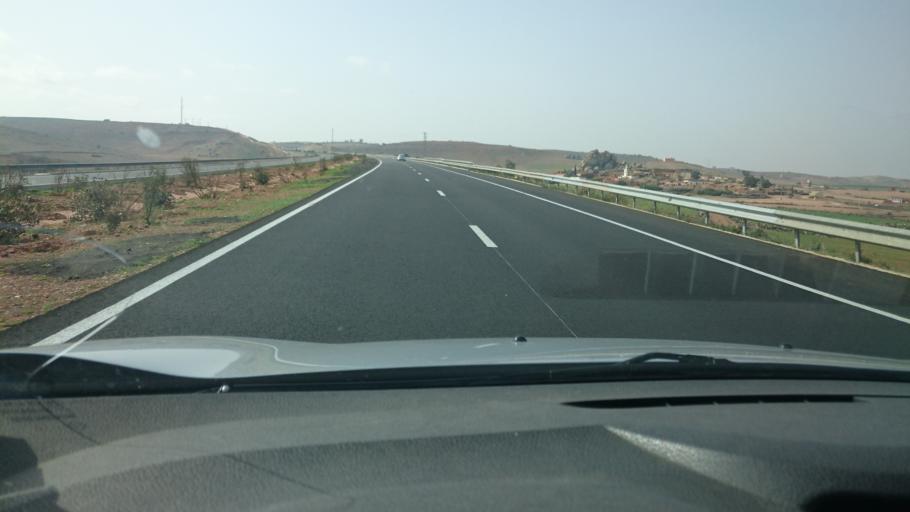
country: MA
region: Marrakech-Tensift-Al Haouz
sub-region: Kelaa-Des-Sraghna
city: Sidi Abdallah
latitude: 32.5445
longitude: -7.9005
